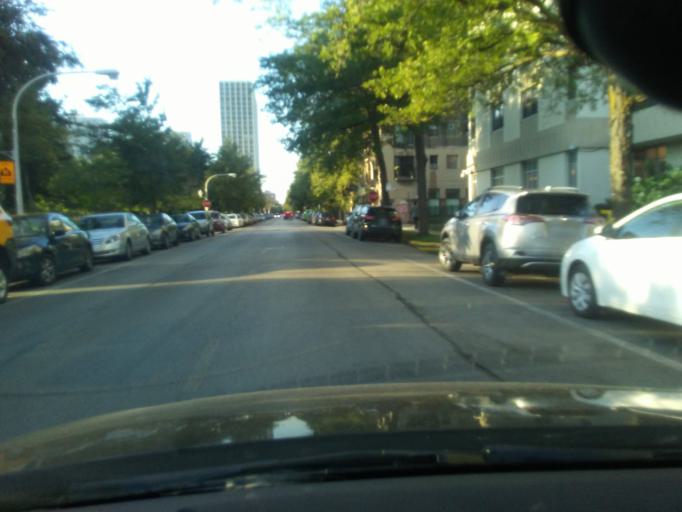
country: US
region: Illinois
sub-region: Cook County
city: Evanston
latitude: 41.9650
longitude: -87.6500
